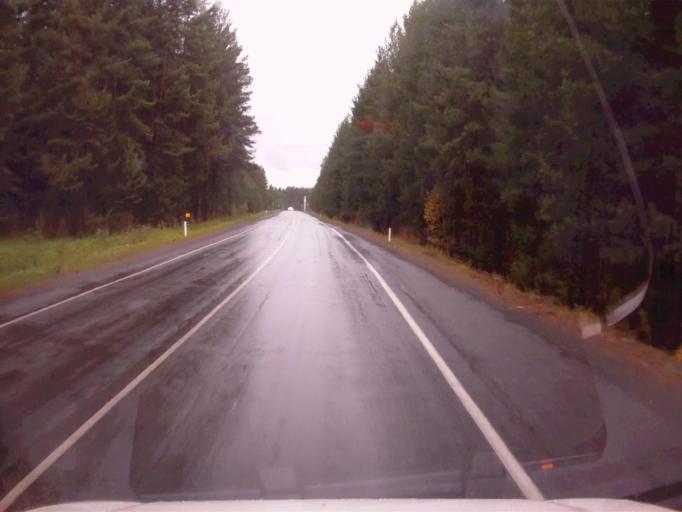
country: RU
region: Chelyabinsk
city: Verkhniy Ufaley
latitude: 56.0261
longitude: 60.2939
